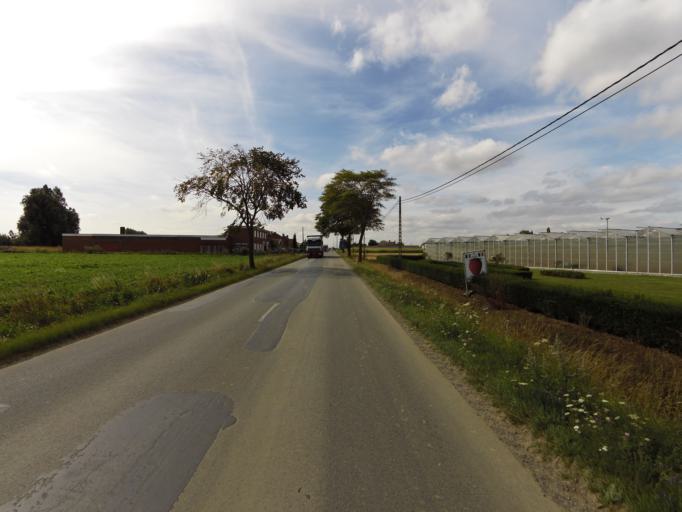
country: BE
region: Flanders
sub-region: Provincie West-Vlaanderen
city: Houthulst
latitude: 50.9420
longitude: 2.9400
